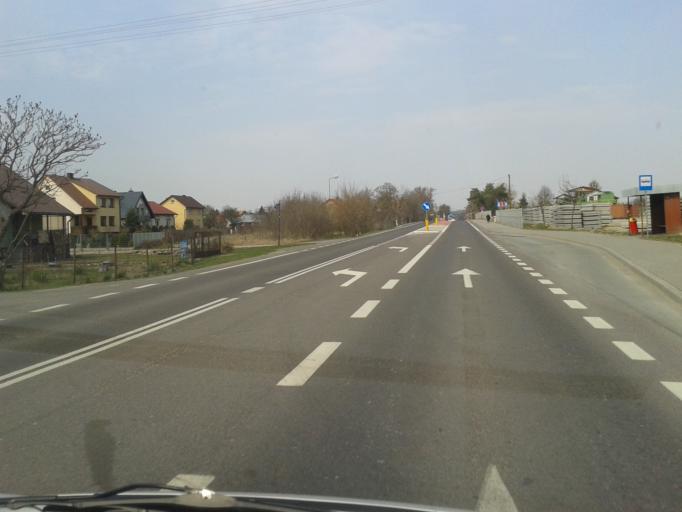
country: PL
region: Lublin Voivodeship
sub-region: Powiat tomaszowski
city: Belzec
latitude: 50.3728
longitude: 23.4545
